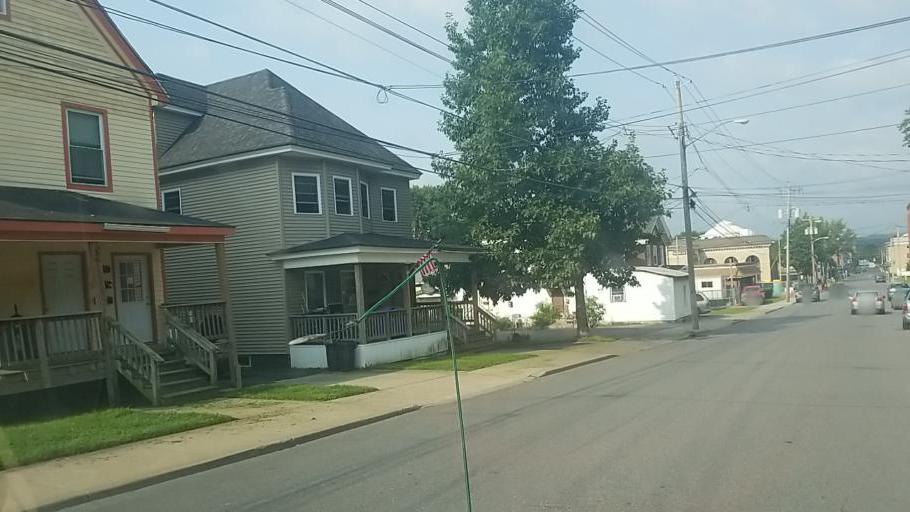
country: US
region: New York
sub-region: Fulton County
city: Gloversville
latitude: 43.0509
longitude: -74.3413
